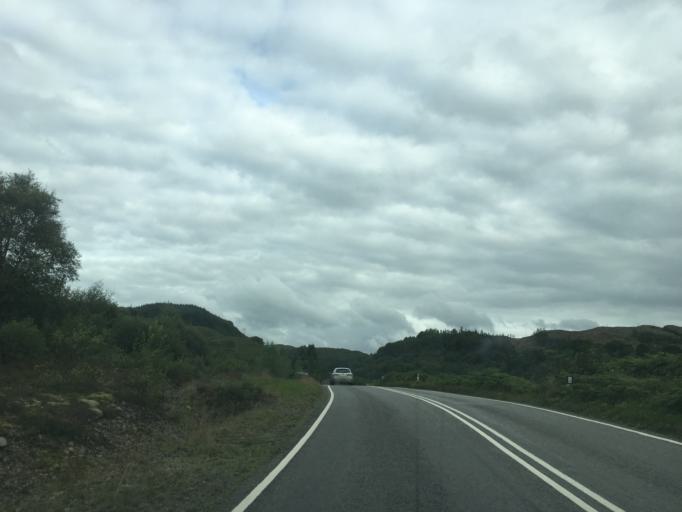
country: GB
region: Scotland
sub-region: Argyll and Bute
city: Oban
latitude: 56.3221
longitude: -5.4975
